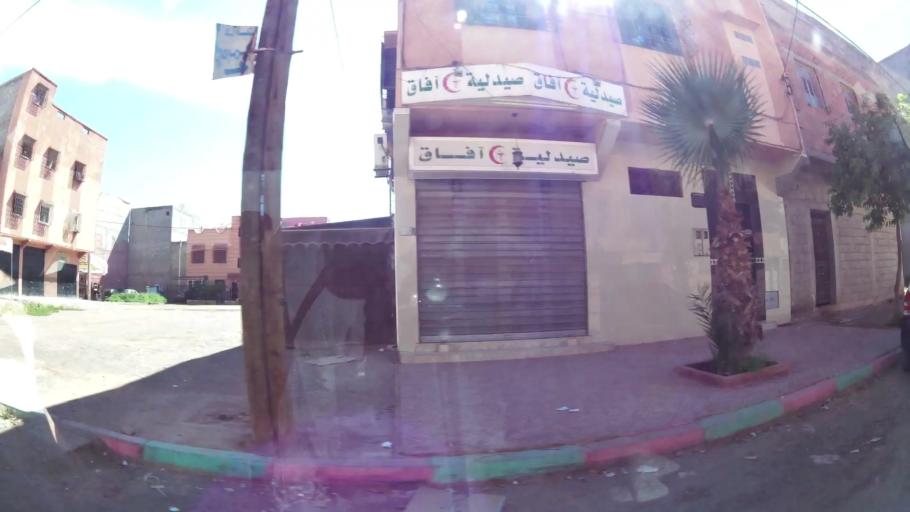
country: MA
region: Marrakech-Tensift-Al Haouz
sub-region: Marrakech
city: Marrakesh
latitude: 31.6418
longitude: -8.1133
